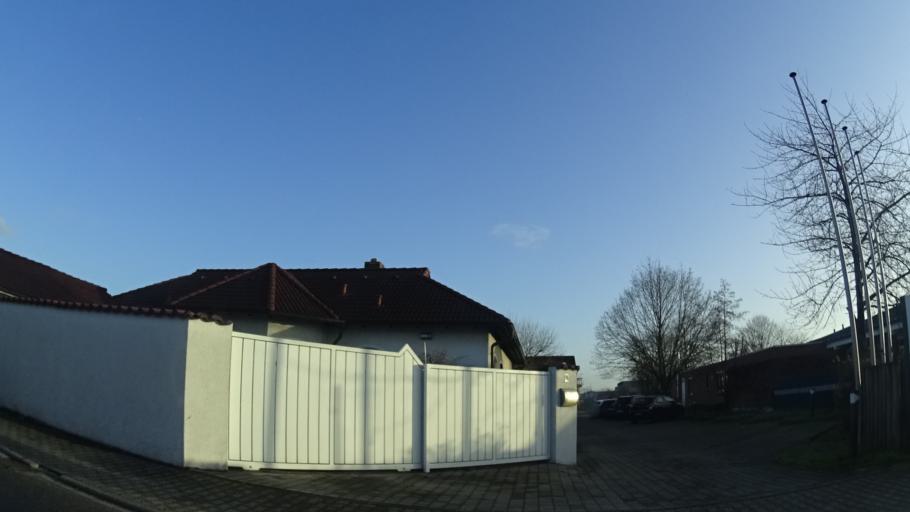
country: DE
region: Baden-Wuerttemberg
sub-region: Karlsruhe Region
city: Forst
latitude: 49.1583
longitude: 8.5714
